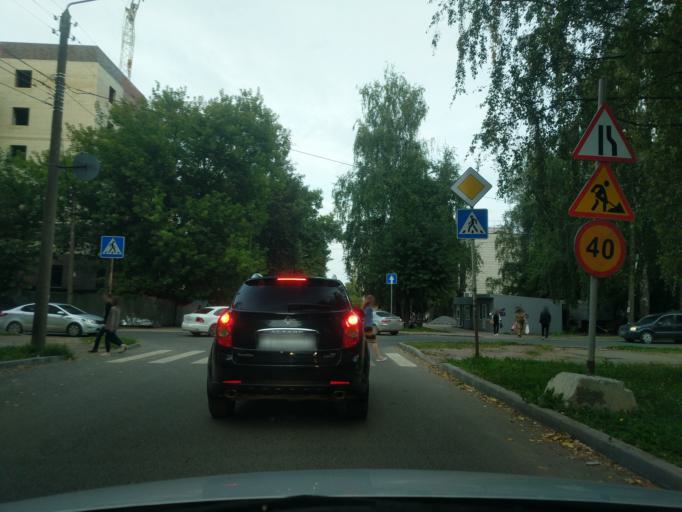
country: RU
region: Kirov
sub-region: Kirovo-Chepetskiy Rayon
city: Kirov
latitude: 58.6116
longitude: 49.6640
